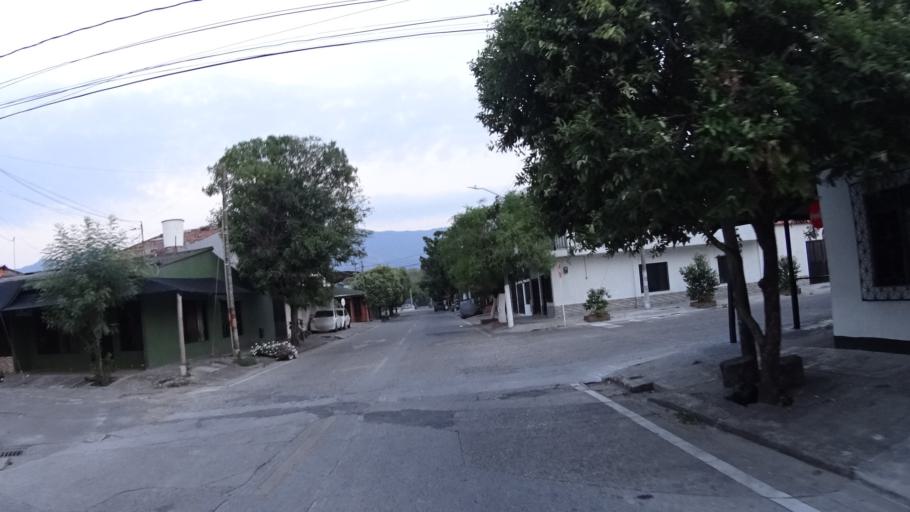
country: CO
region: Caldas
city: La Dorada
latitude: 5.4445
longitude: -74.6602
